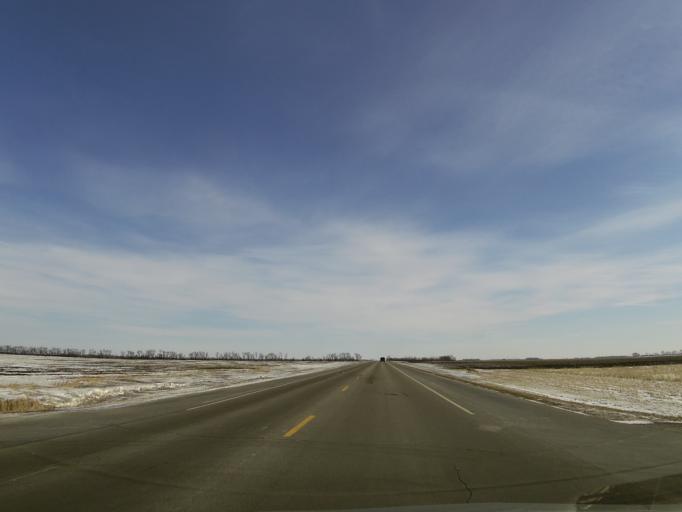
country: US
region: North Dakota
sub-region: Walsh County
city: Grafton
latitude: 48.4125
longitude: -97.3651
